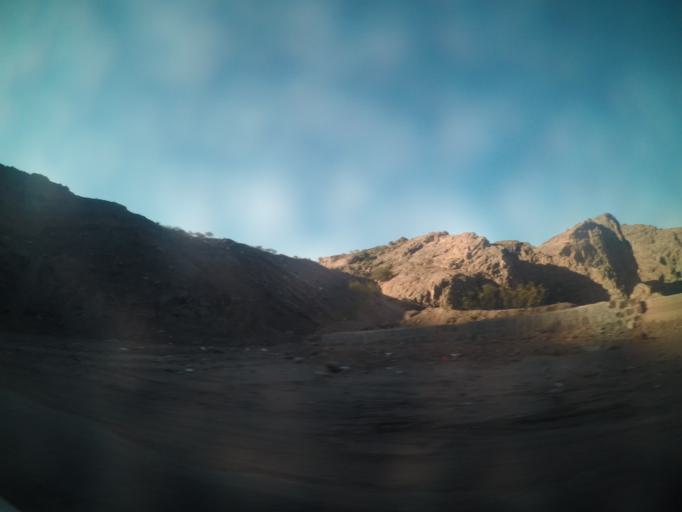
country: YE
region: Ad Dali'
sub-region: Ad Dhale'e
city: Dhalie
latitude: 13.6711
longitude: 44.7670
